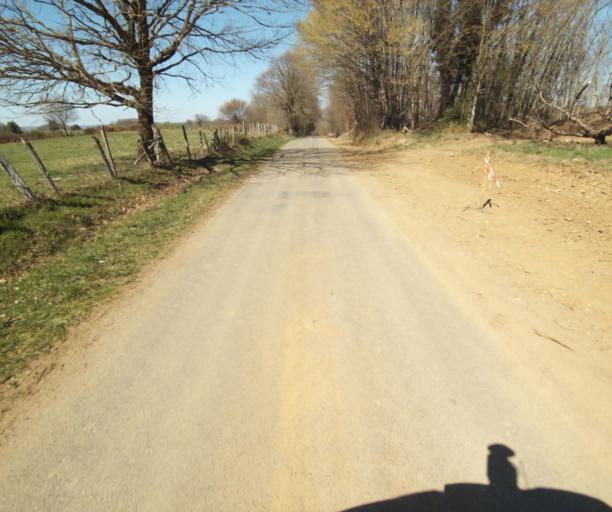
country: FR
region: Limousin
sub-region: Departement de la Correze
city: Saint-Clement
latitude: 45.3776
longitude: 1.6785
